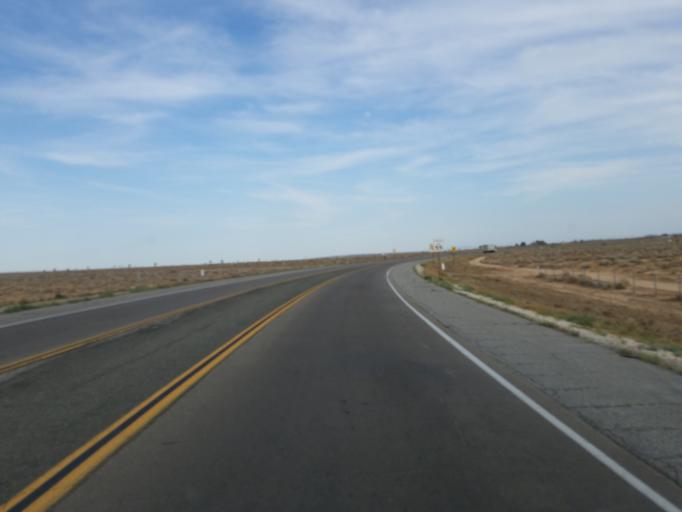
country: US
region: California
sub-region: Kern County
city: Boron
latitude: 35.0096
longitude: -117.6244
